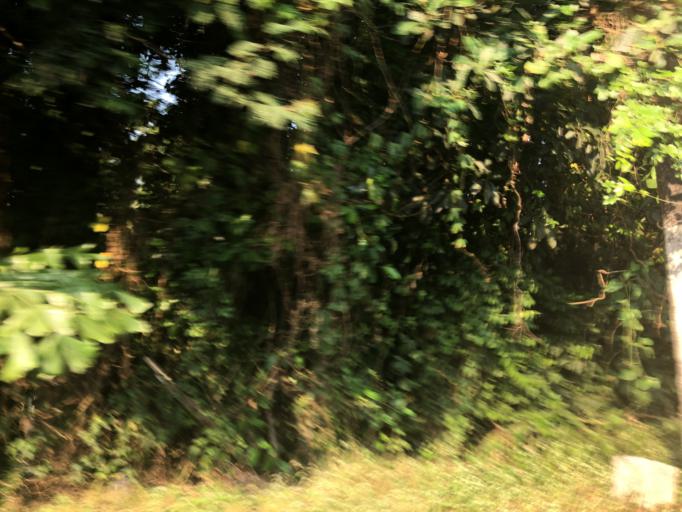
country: IN
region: Karnataka
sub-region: Dakshina Kannada
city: Ullal
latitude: 12.8146
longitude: 74.8551
